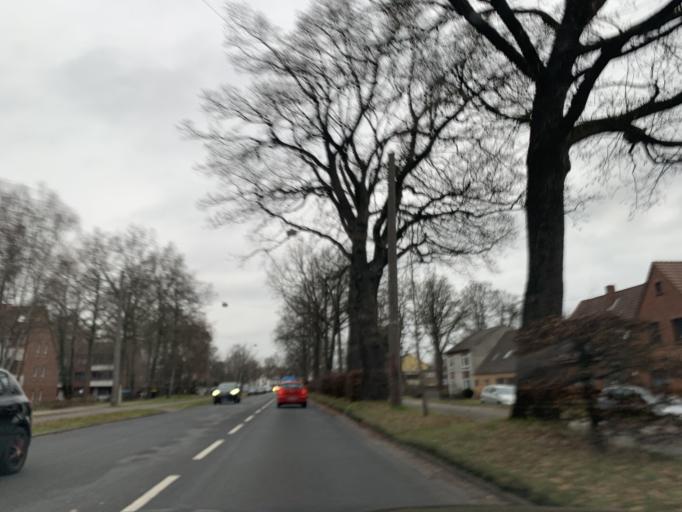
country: DE
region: Lower Saxony
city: Ritterhude
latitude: 53.1486
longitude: 8.7110
